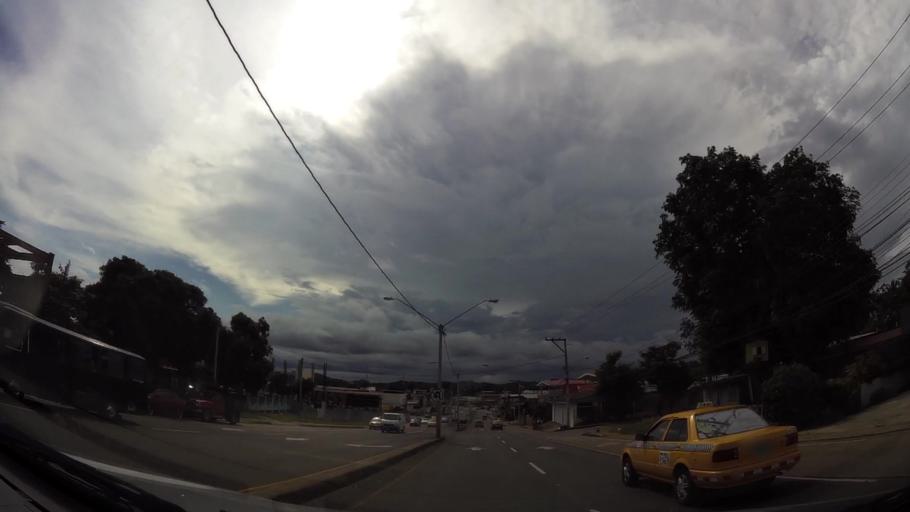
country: PA
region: Panama
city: La Chorrera
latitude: 8.8726
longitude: -79.7973
